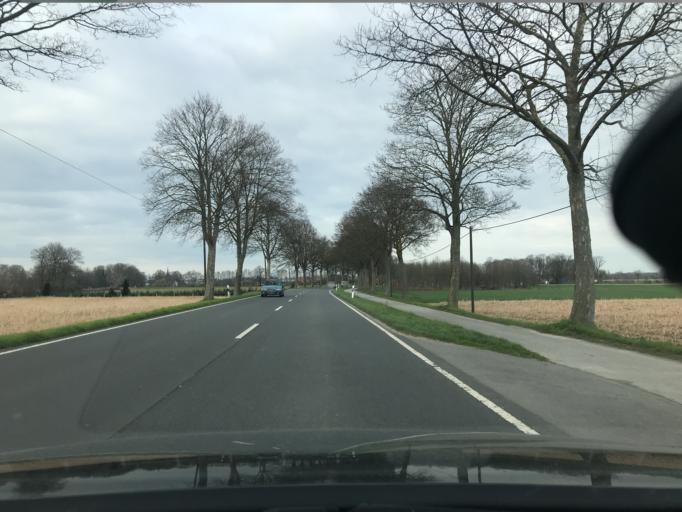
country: DE
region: North Rhine-Westphalia
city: Kempen
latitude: 51.4216
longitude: 6.4184
